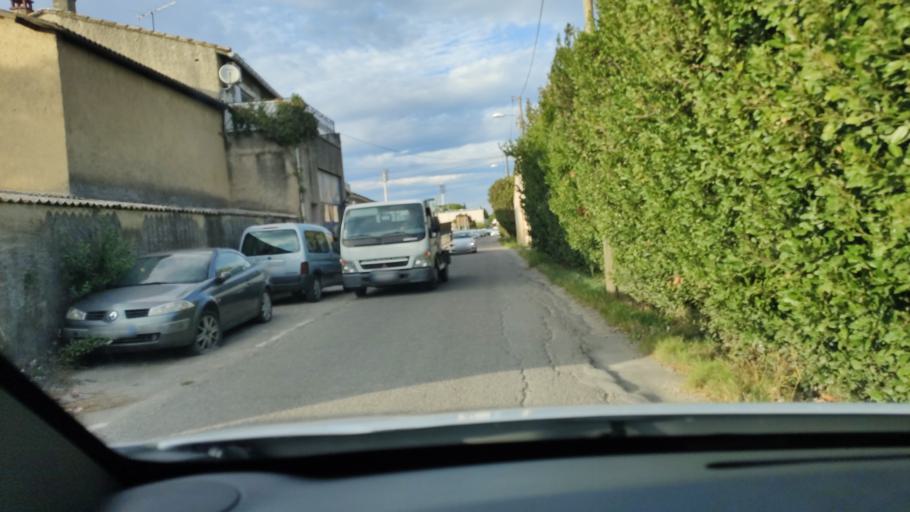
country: FR
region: Provence-Alpes-Cote d'Azur
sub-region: Departement du Vaucluse
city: Montfavet
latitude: 43.9243
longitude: 4.8439
